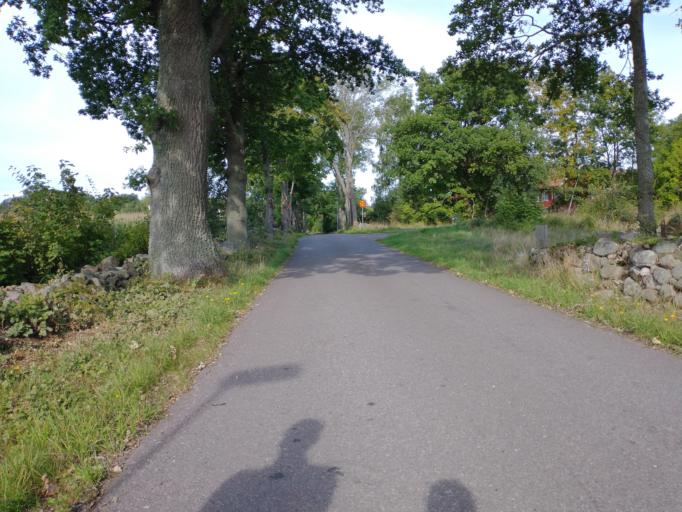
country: SE
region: Kalmar
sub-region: Kalmar Kommun
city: Lindsdal
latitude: 56.7792
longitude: 16.3042
